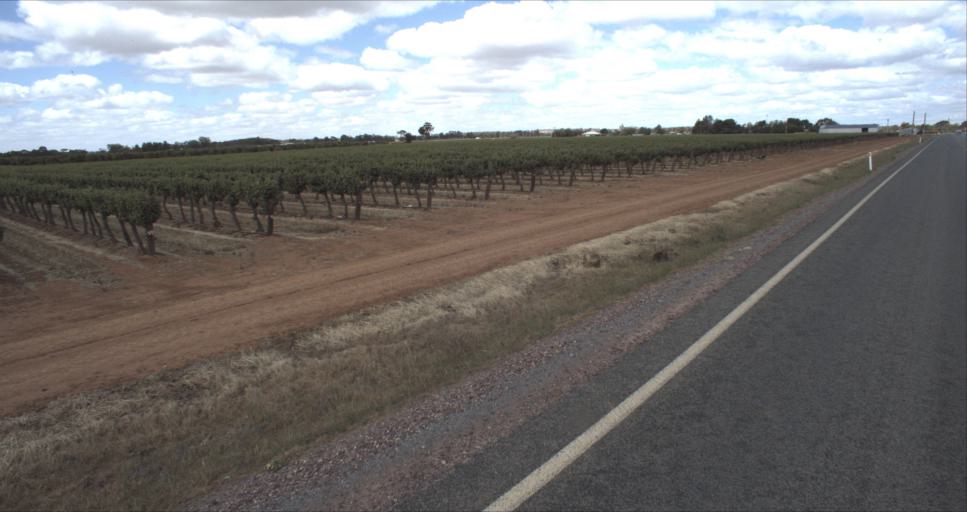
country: AU
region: New South Wales
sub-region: Leeton
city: Leeton
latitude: -34.5827
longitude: 146.4016
